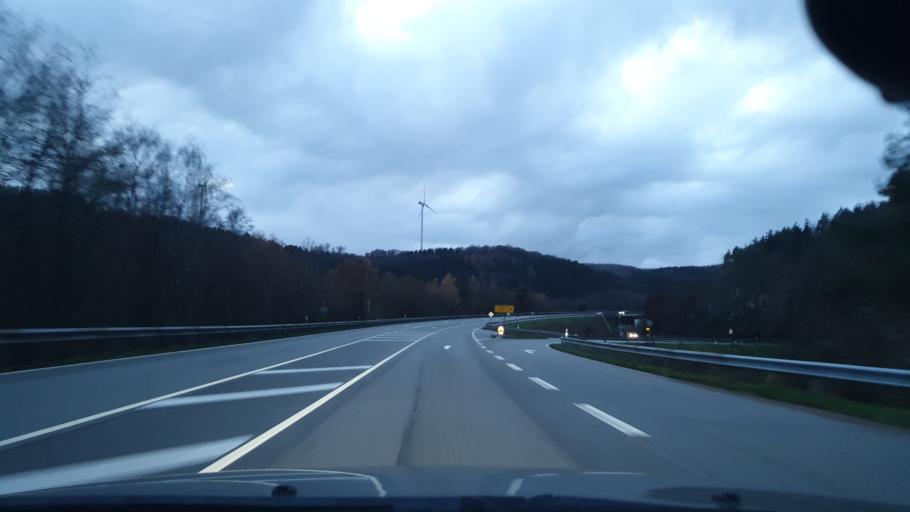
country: DE
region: Rheinland-Pfalz
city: Steinalben
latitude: 49.3135
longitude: 7.6594
